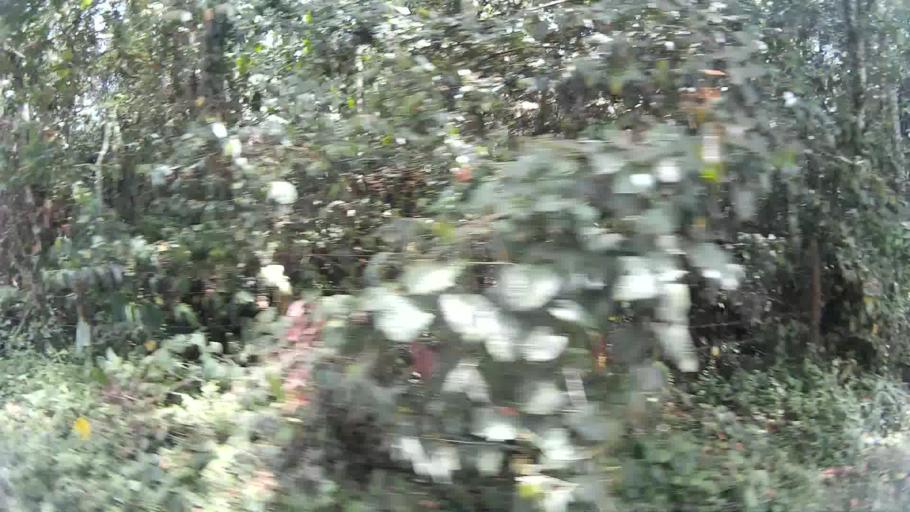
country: CO
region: Quindio
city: Filandia
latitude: 4.7115
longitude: -75.6516
